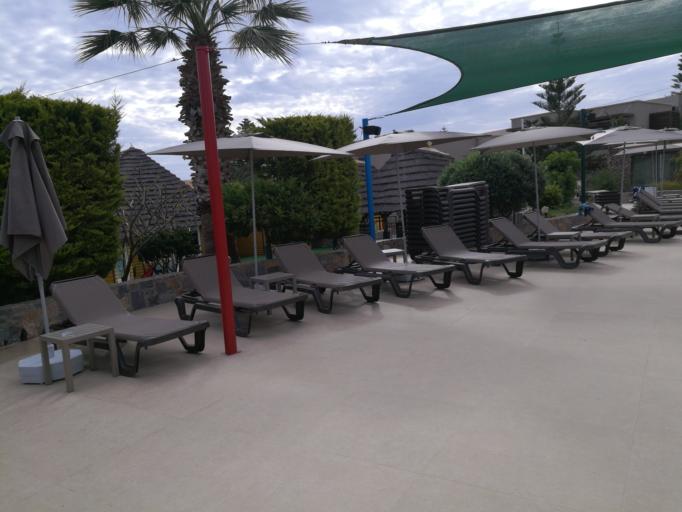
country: GR
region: Crete
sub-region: Nomos Irakleiou
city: Stalis
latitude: 35.3040
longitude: 25.4204
